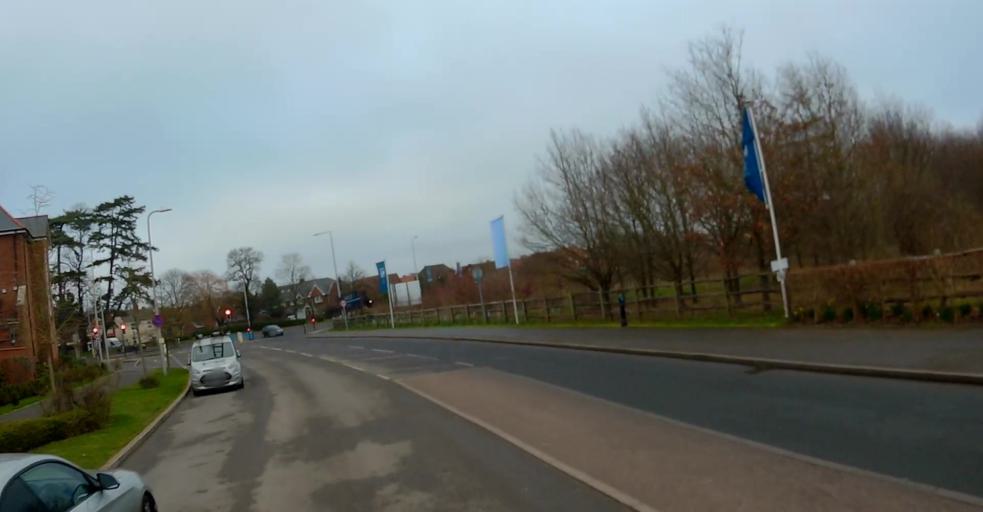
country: GB
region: England
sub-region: Bracknell Forest
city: Binfield
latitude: 51.4115
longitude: -0.8058
